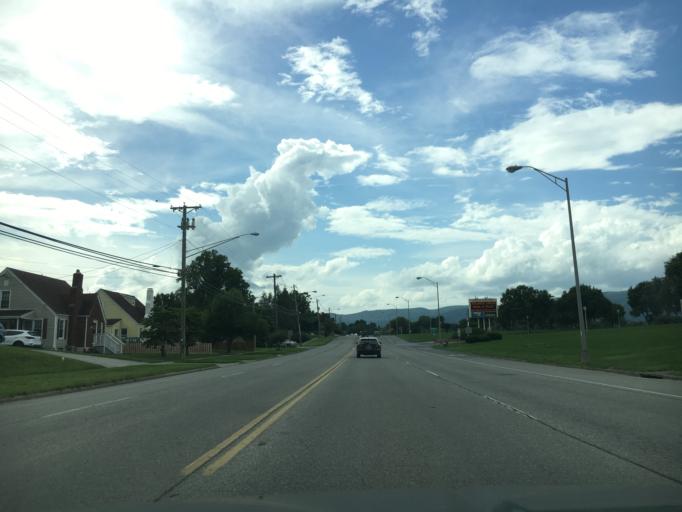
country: US
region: Virginia
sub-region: City of Salem
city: Salem
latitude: 37.2833
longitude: -80.0401
